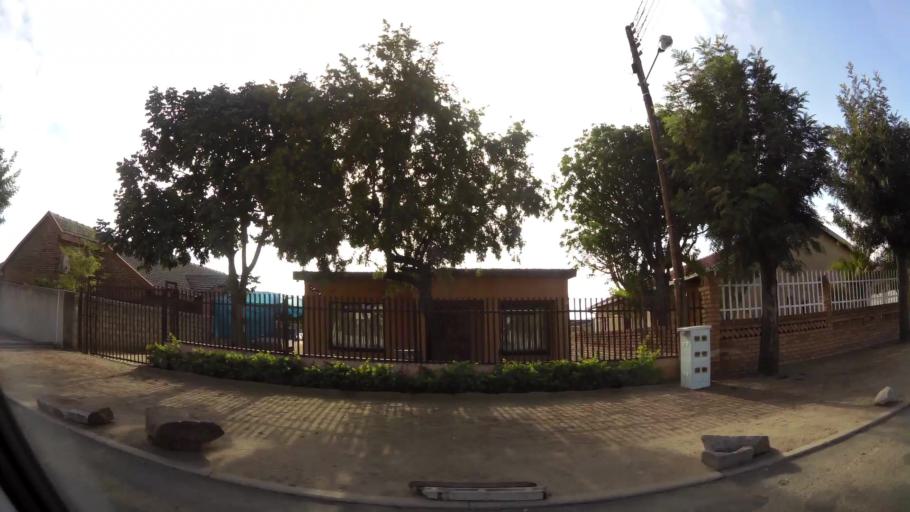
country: ZA
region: Limpopo
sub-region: Capricorn District Municipality
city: Polokwane
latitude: -23.8439
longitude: 29.3866
